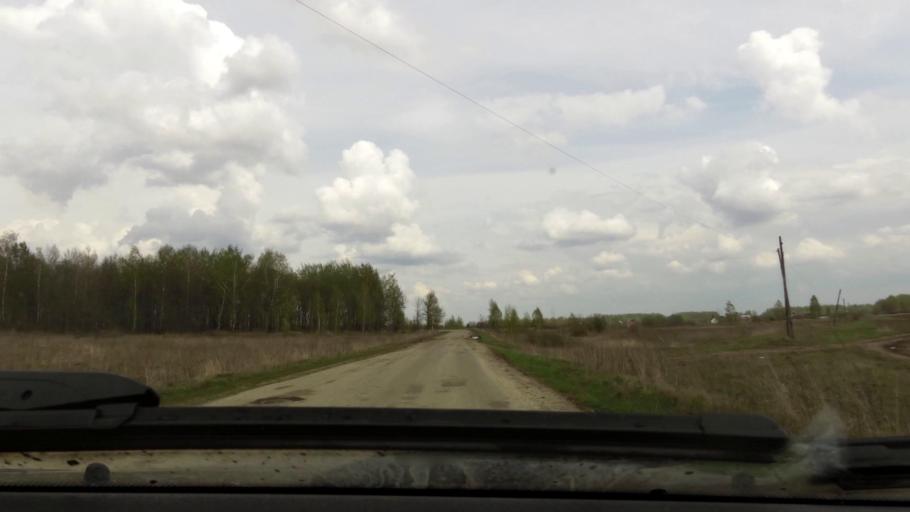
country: RU
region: Rjazan
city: Bagramovo
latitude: 54.7034
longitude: 39.3154
